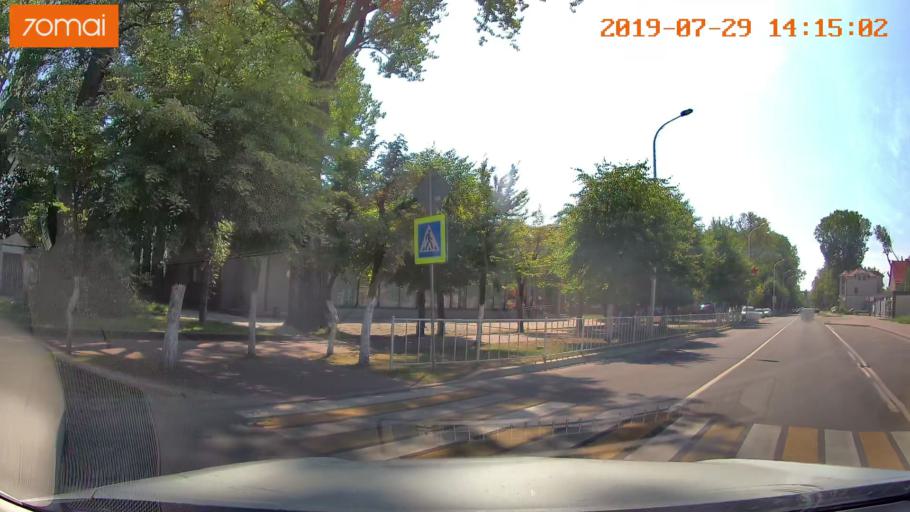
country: RU
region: Kaliningrad
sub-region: Gorod Kaliningrad
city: Baltiysk
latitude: 54.6485
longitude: 19.9022
